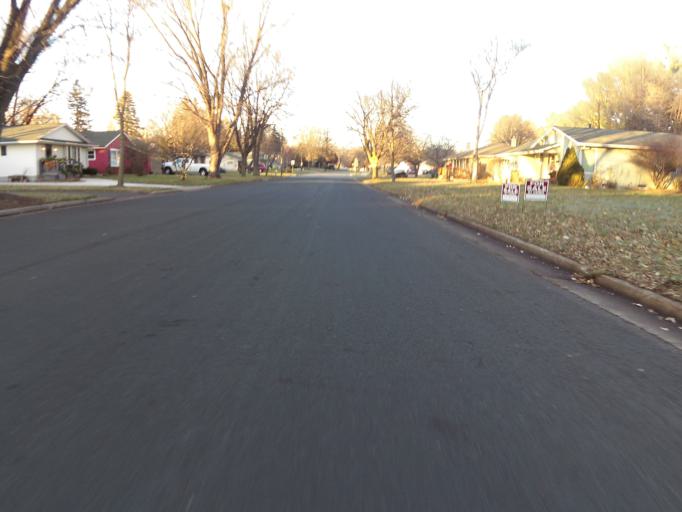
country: US
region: Wisconsin
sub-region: Pierce County
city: River Falls
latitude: 44.8563
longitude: -92.6153
